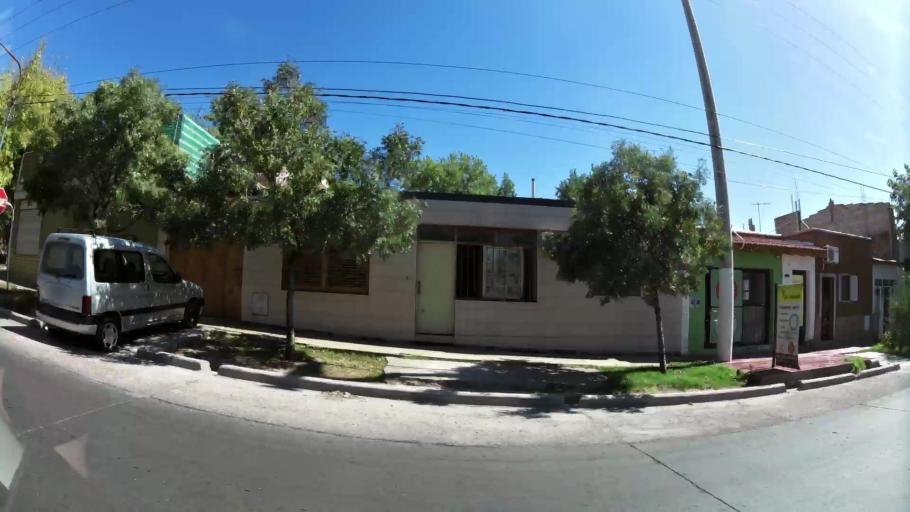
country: AR
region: Mendoza
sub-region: Departamento de Godoy Cruz
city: Godoy Cruz
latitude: -32.9229
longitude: -68.8618
